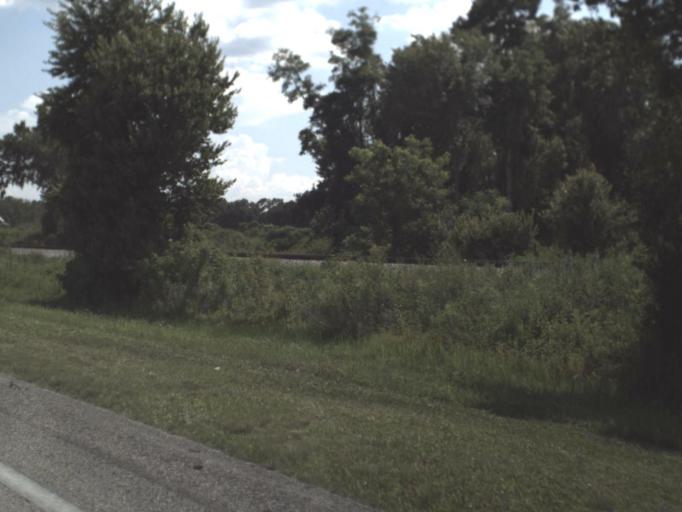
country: US
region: Florida
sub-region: Alachua County
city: Hawthorne
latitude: 29.5545
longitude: -82.0975
